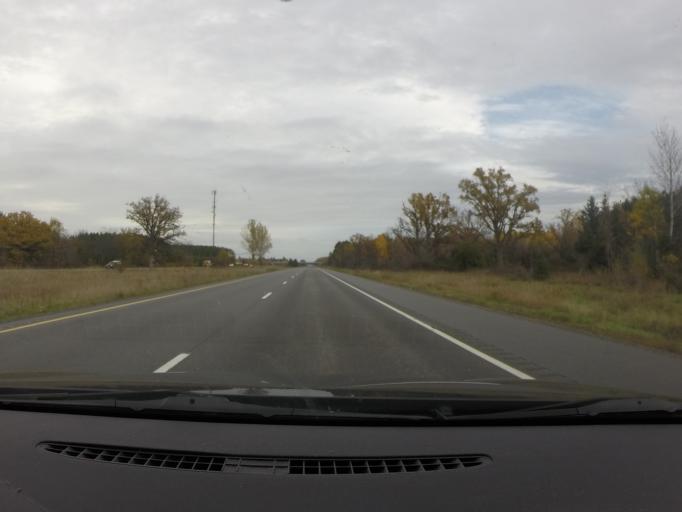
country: CA
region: Ontario
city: Carleton Place
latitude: 45.3228
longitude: -76.1104
